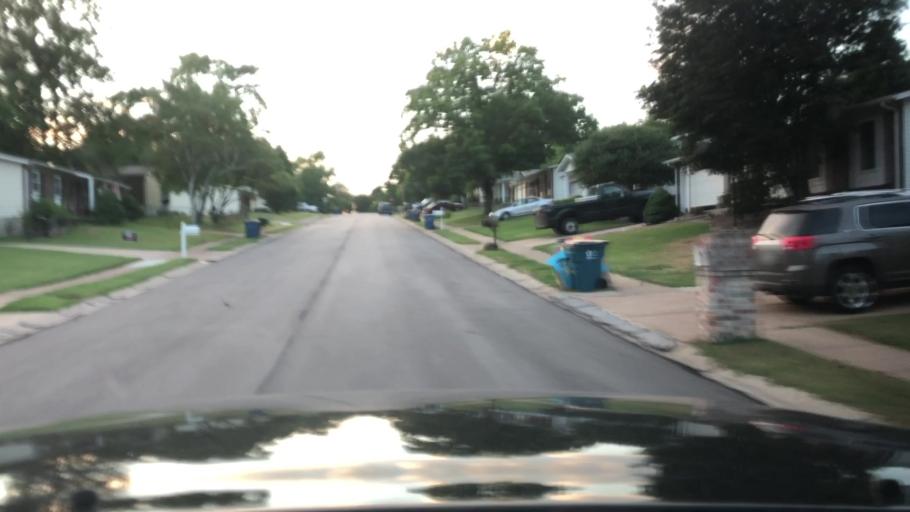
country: US
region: Missouri
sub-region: Saint Charles County
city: Saint Charles
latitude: 38.8114
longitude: -90.5063
